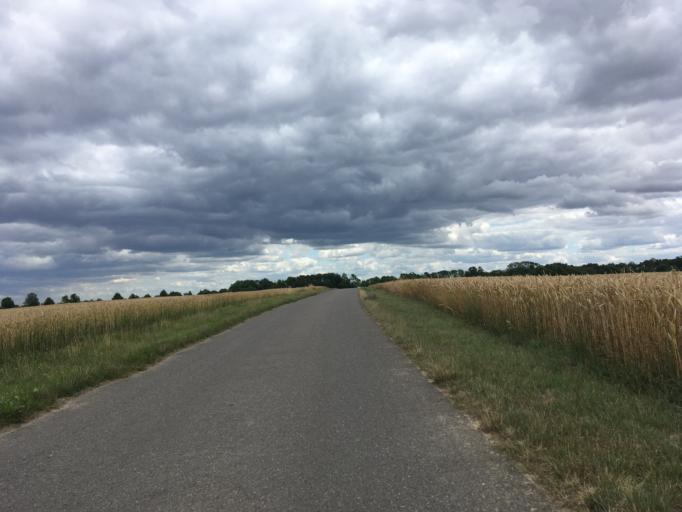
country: DE
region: Brandenburg
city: Gramzow
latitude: 53.2538
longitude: 13.9920
